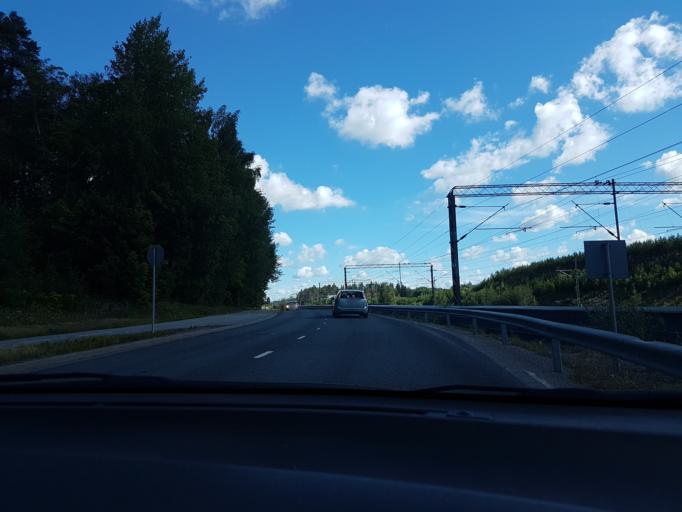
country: FI
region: Uusimaa
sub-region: Helsinki
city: Kerava
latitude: 60.3729
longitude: 25.0942
